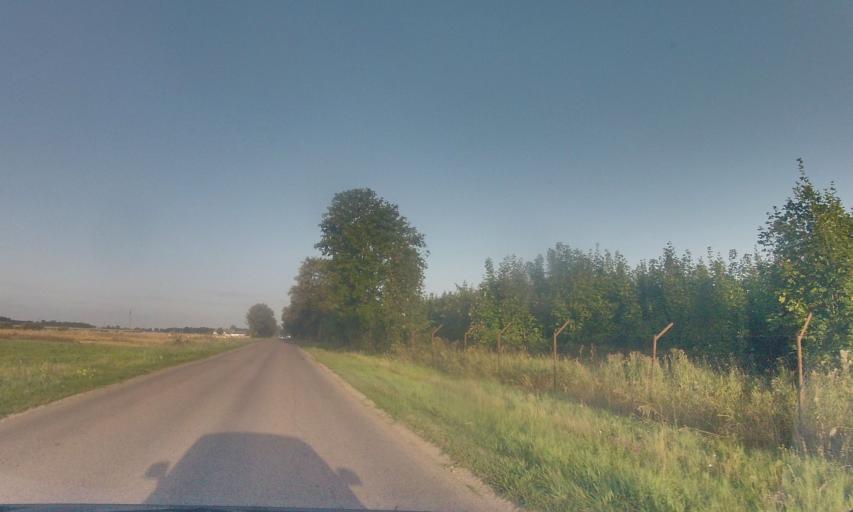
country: PL
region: Masovian Voivodeship
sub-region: Powiat mlawski
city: Szrensk
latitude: 52.9972
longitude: 20.2204
